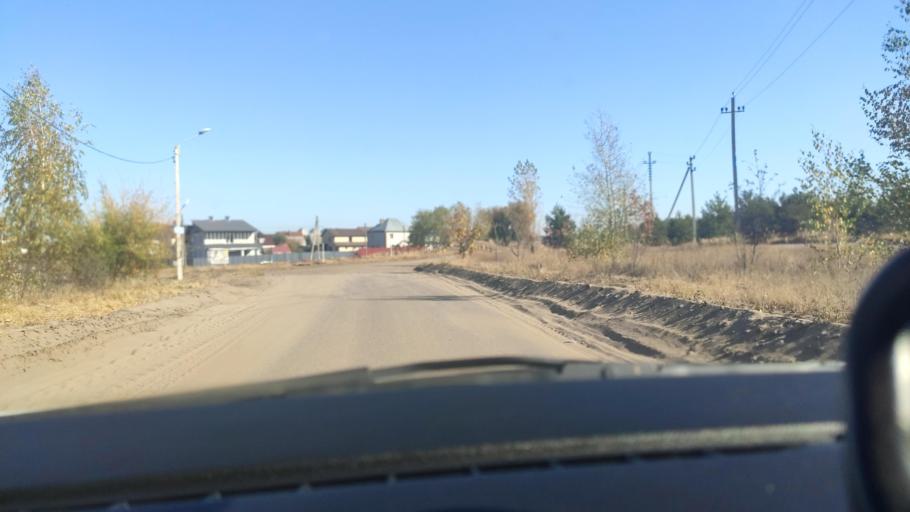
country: RU
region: Voronezj
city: Pridonskoy
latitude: 51.6280
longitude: 39.0936
